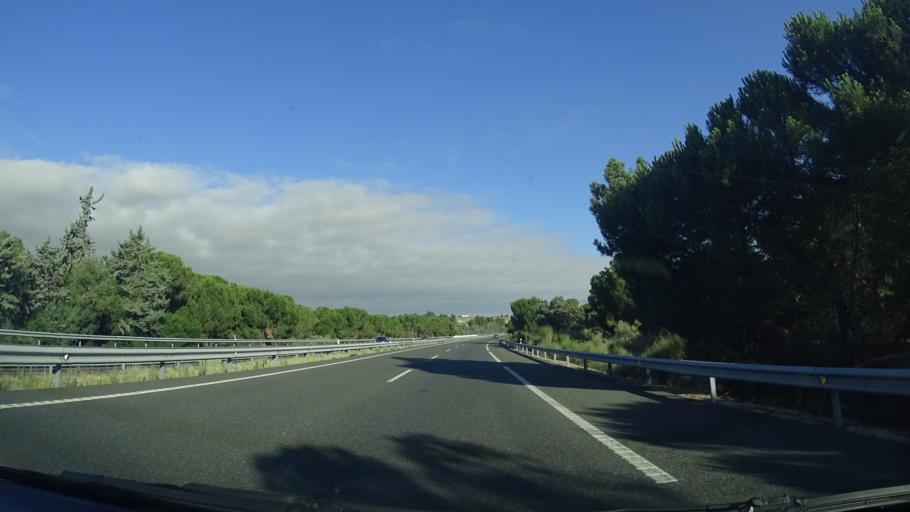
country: ES
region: Castille and Leon
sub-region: Provincia de Avila
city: Sanchidrian
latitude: 40.8618
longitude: -4.5595
